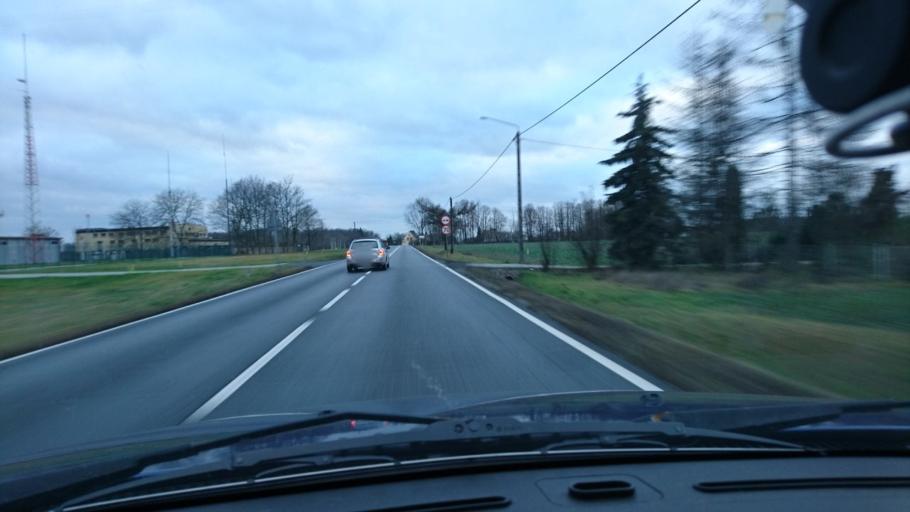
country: PL
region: Lodz Voivodeship
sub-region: Powiat wieruszowski
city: Boleslawiec
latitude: 51.1616
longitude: 18.1582
